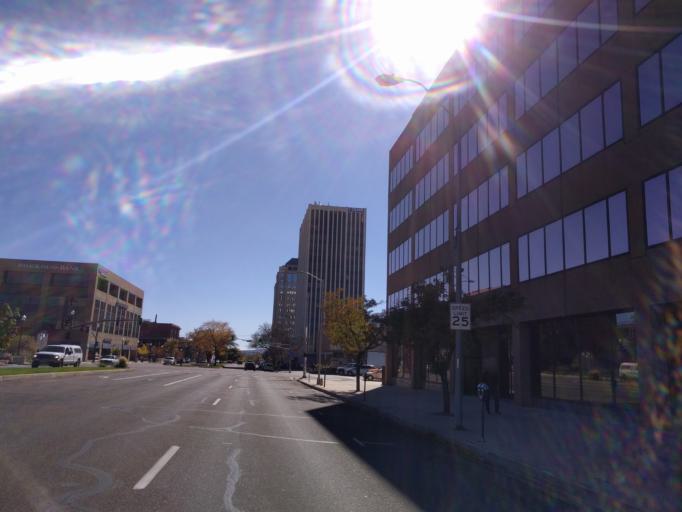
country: US
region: Colorado
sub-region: El Paso County
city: Colorado Springs
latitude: 38.8362
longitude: -104.8254
